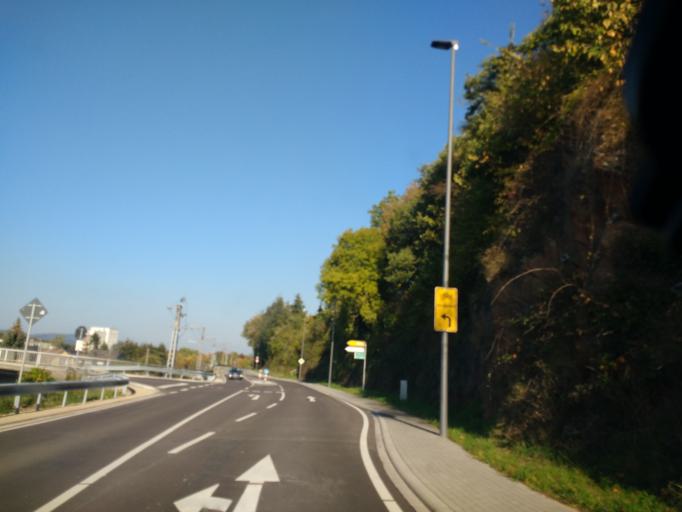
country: DE
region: Rheinland-Pfalz
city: Konz
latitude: 49.7109
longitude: 6.5985
